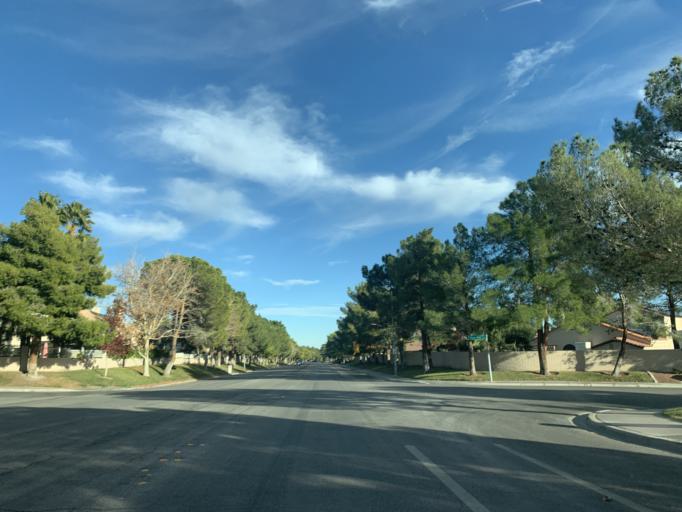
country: US
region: Nevada
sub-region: Clark County
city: Summerlin South
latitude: 36.1334
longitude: -115.3016
